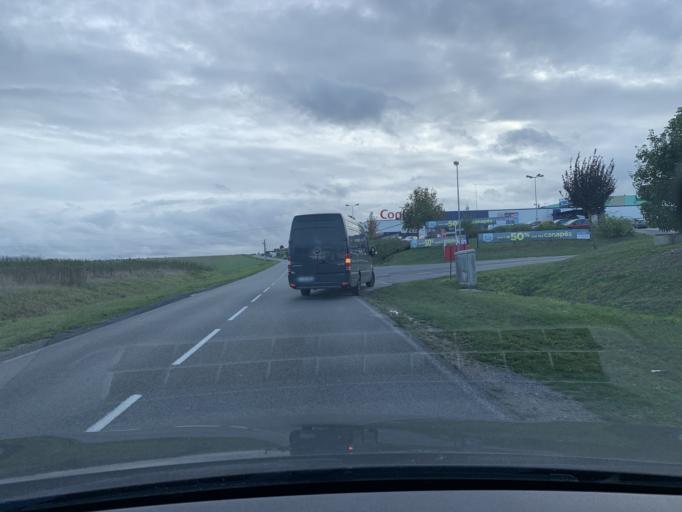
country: FR
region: Nord-Pas-de-Calais
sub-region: Departement du Nord
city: Proville
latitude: 50.1480
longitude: 3.2169
